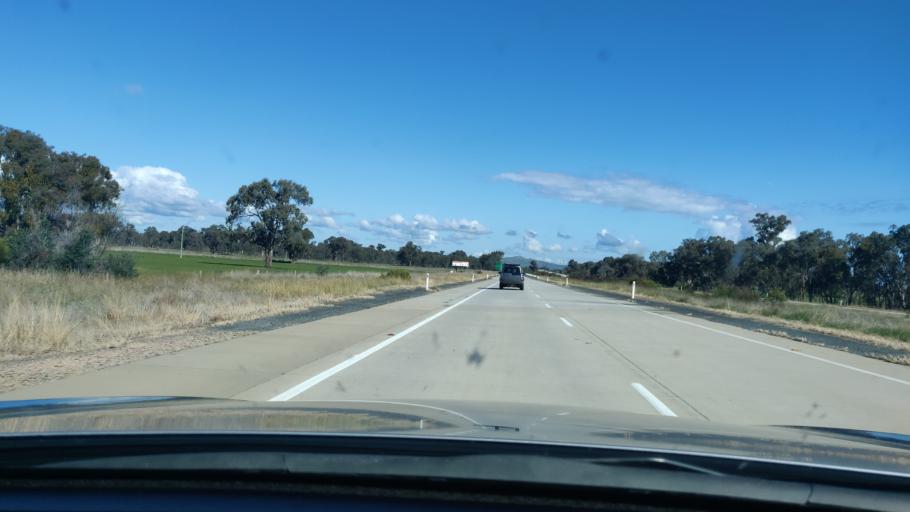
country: AU
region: New South Wales
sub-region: Greater Hume Shire
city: Holbrook
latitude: -35.6909
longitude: 147.3486
